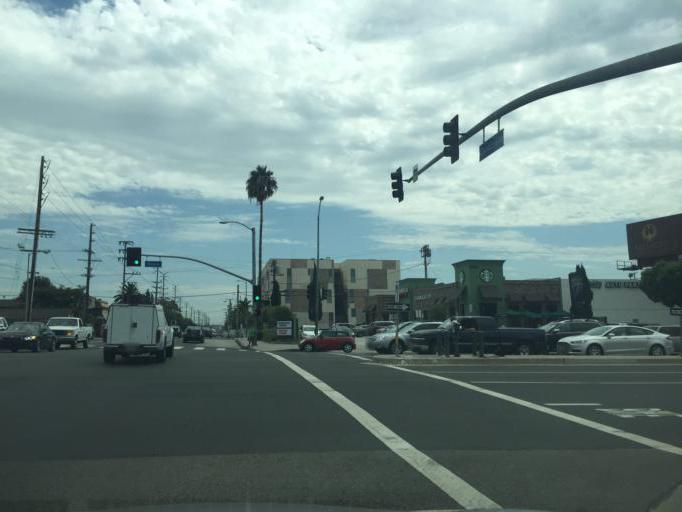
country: US
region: California
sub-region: Los Angeles County
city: Marina del Rey
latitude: 34.0039
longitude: -118.4338
